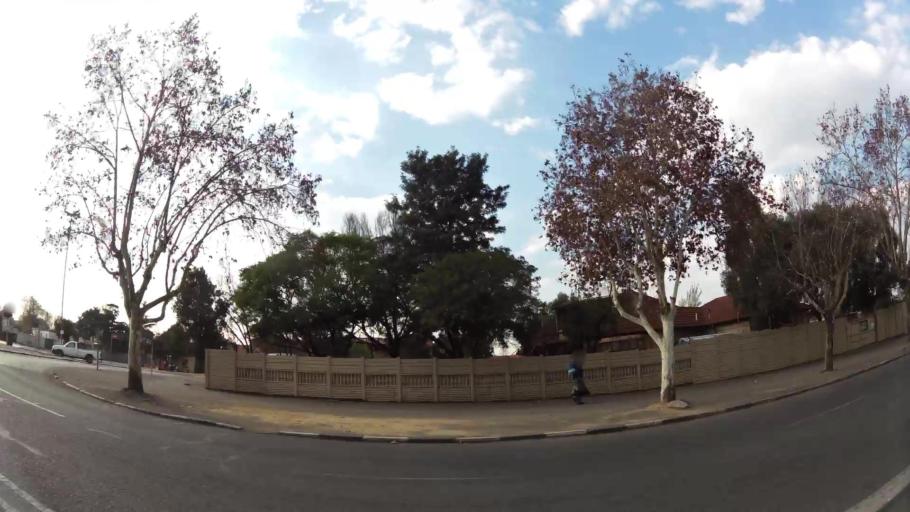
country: ZA
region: Gauteng
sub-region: Ekurhuleni Metropolitan Municipality
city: Germiston
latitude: -26.2241
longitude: 28.1732
